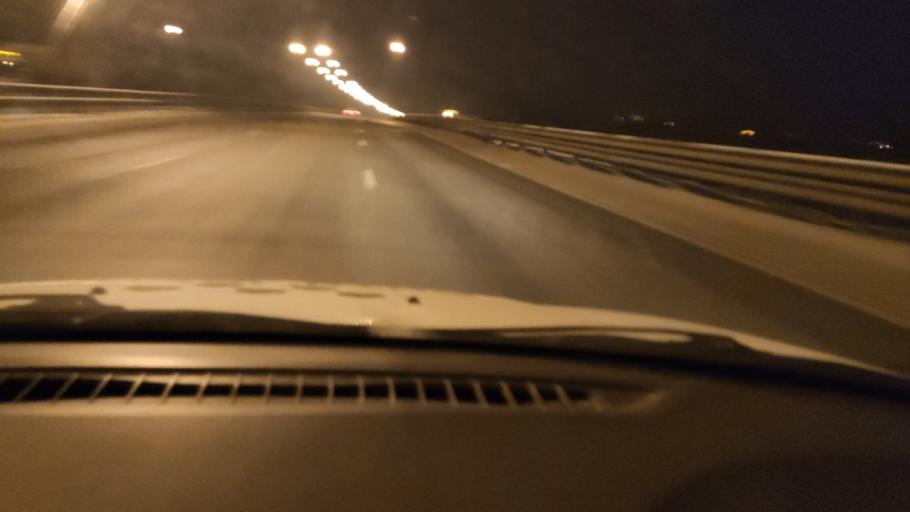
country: RU
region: Perm
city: Bershet'
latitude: 57.7061
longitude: 56.3691
